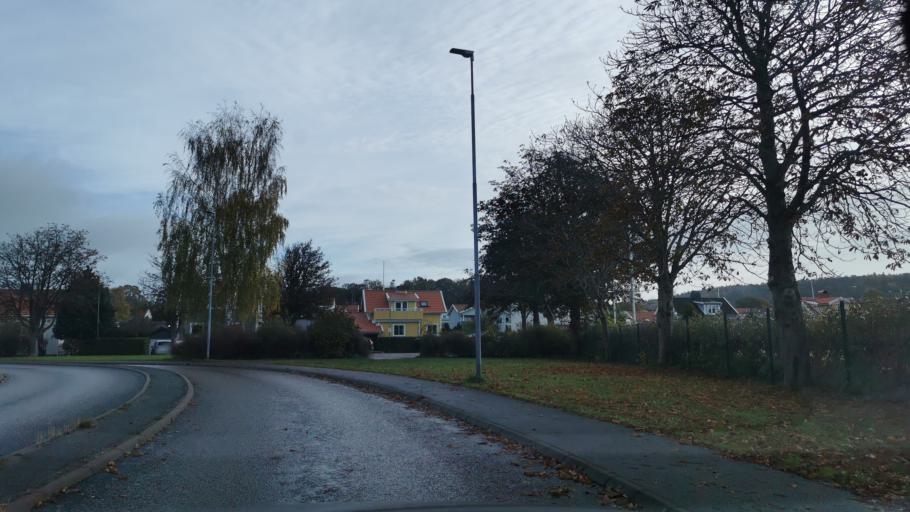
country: SE
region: Vaestra Goetaland
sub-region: Partille Kommun
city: Partille
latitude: 57.7255
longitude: 12.0792
